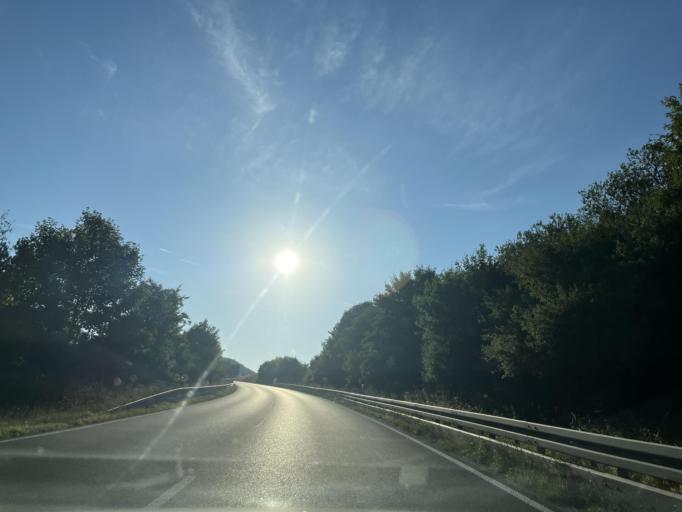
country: DE
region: Baden-Wuerttemberg
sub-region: Tuebingen Region
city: Burladingen
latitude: 48.2928
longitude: 9.0849
